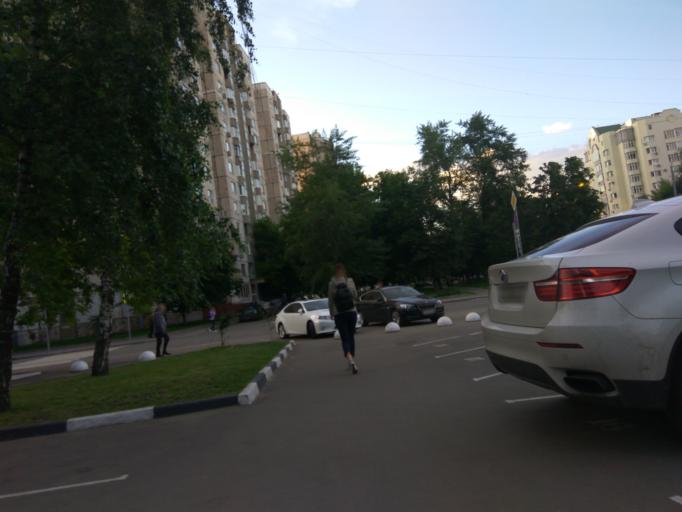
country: RU
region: Moscow
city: Zamoskvorech'ye
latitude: 55.7235
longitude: 37.6217
